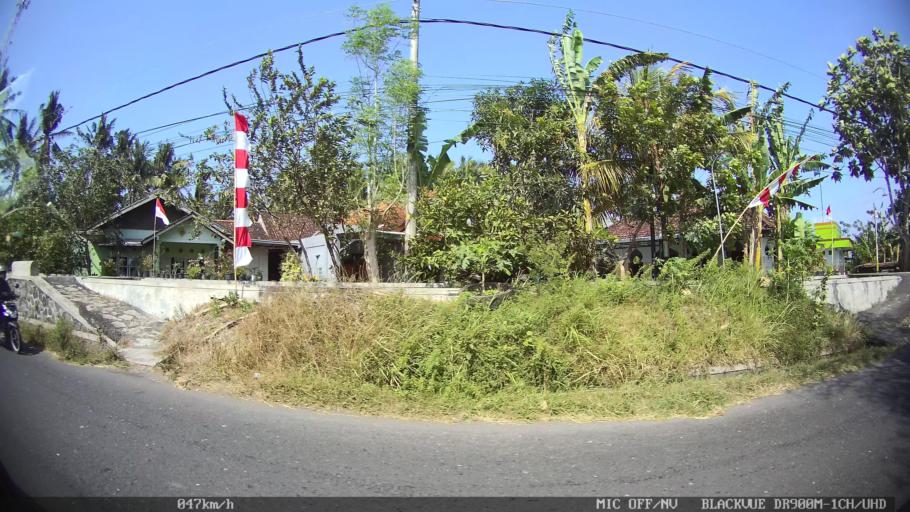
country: ID
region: Daerah Istimewa Yogyakarta
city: Srandakan
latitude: -7.9205
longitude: 110.1836
